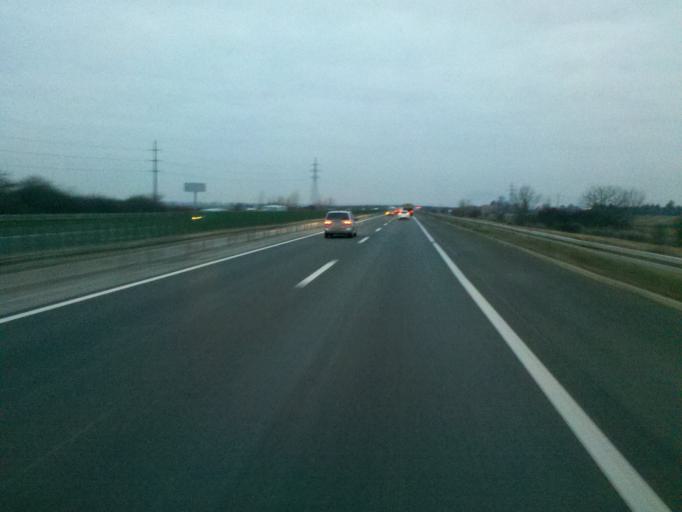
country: HR
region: Grad Zagreb
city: Zadvorsko
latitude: 45.7508
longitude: 15.9505
